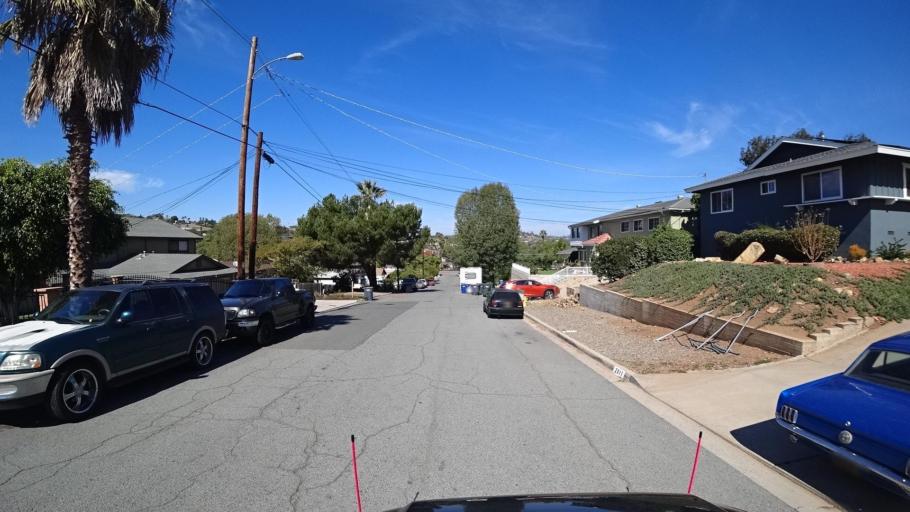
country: US
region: California
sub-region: San Diego County
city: Spring Valley
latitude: 32.7260
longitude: -117.0125
